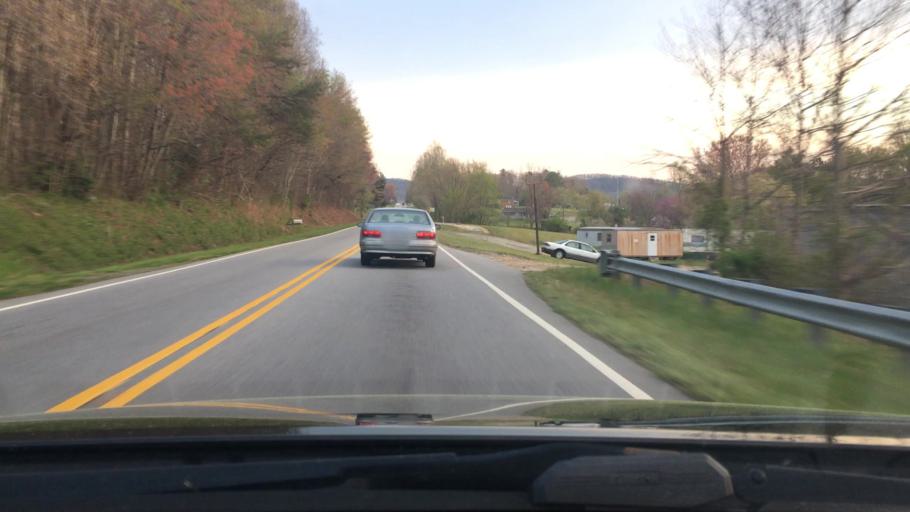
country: US
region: North Carolina
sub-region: McDowell County
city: West Marion
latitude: 35.6067
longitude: -81.9848
